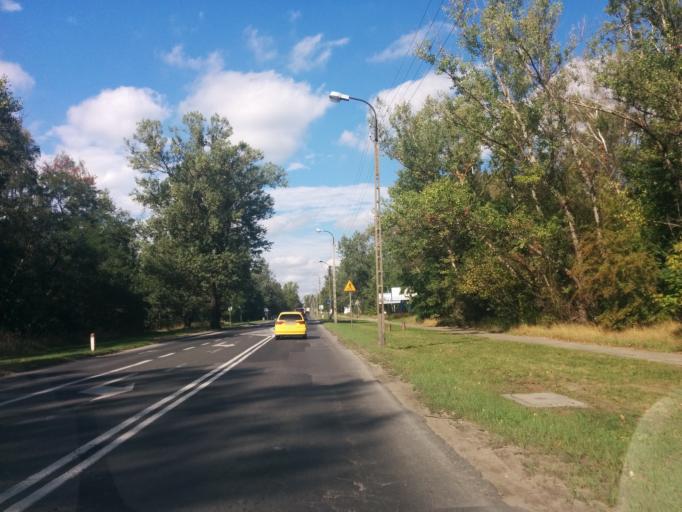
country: PL
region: Masovian Voivodeship
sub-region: Warszawa
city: Bialoleka
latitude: 52.3054
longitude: 21.0081
